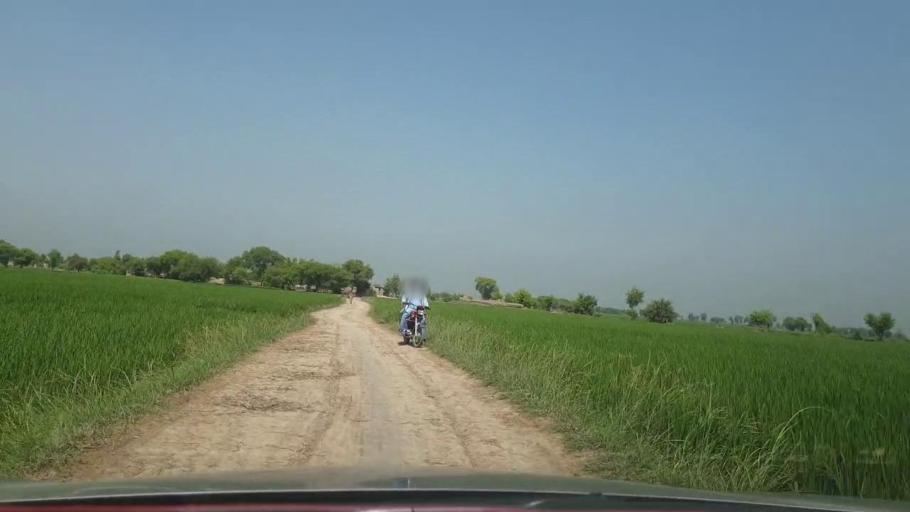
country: PK
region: Sindh
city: Kambar
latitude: 27.5932
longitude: 67.9082
